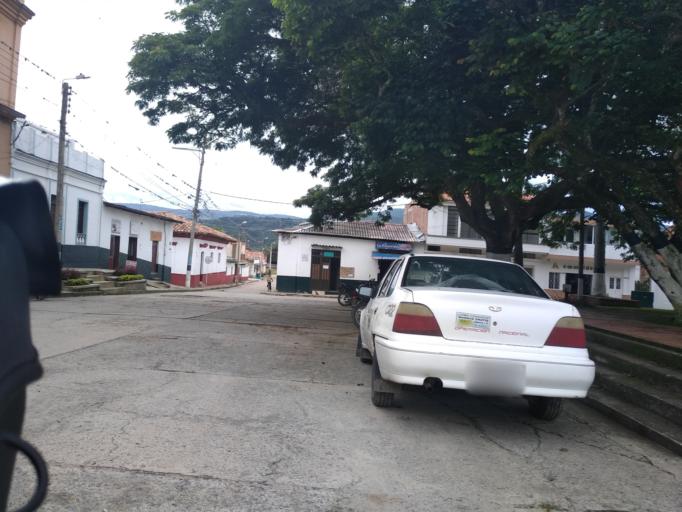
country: CO
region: Santander
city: Guepsa
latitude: 6.0256
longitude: -73.5722
